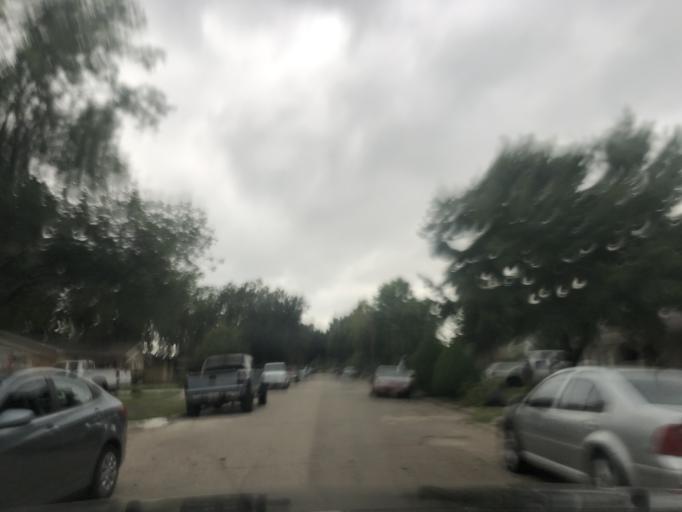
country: US
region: Texas
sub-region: Dallas County
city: Garland
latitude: 32.8745
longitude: -96.6458
